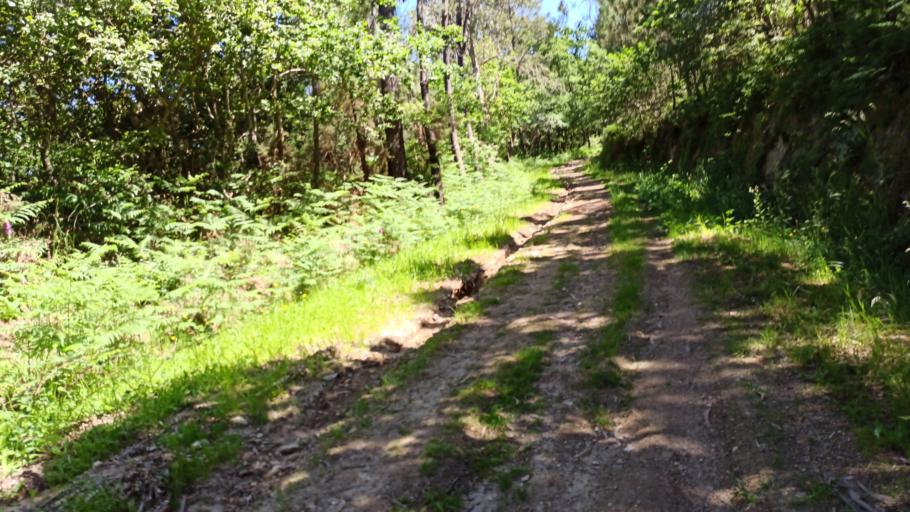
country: ES
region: Galicia
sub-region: Provincia da Coruna
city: Negreira
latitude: 42.9182
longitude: -8.7255
